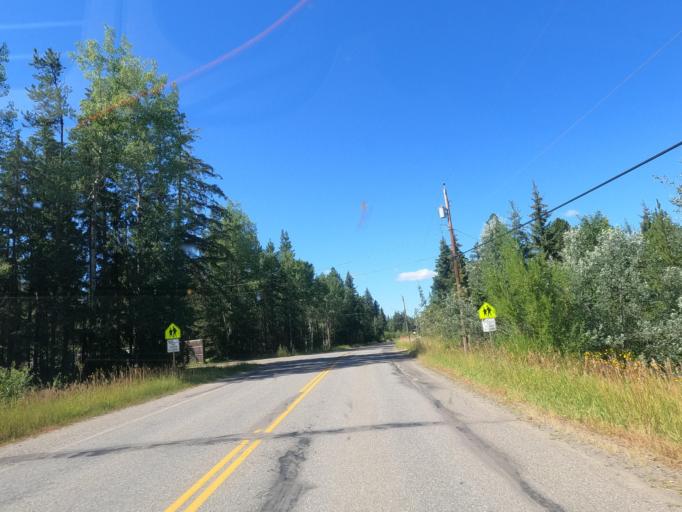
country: CA
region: British Columbia
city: Quesnel
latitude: 53.0218
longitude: -122.4505
